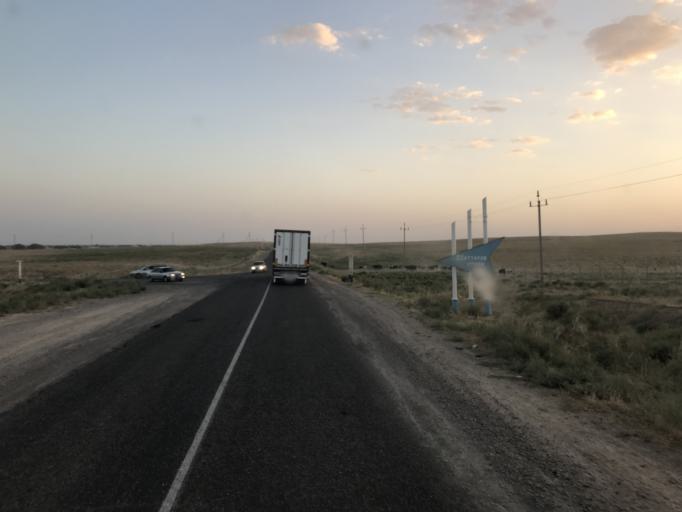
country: UZ
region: Toshkent
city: Amir Timur
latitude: 41.3498
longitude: 68.7097
